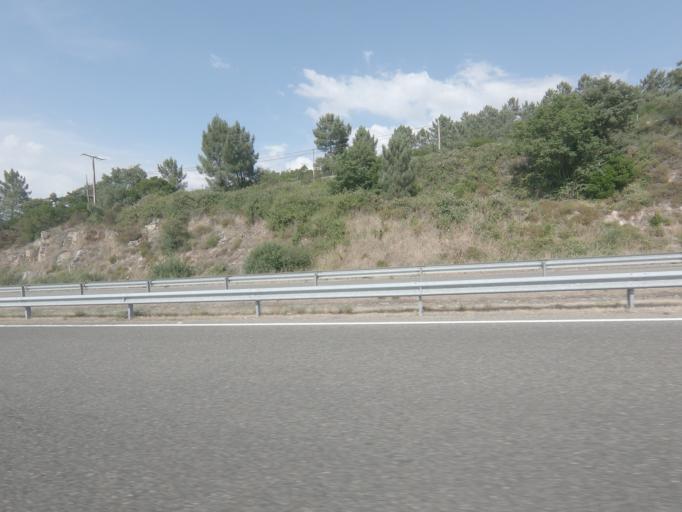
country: ES
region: Galicia
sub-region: Provincia de Ourense
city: Ourense
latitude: 42.2841
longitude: -7.8743
